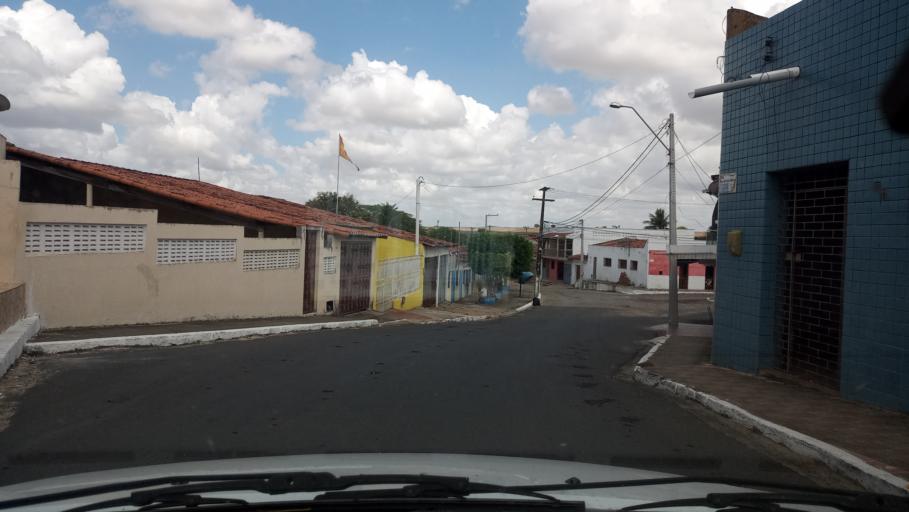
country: BR
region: Rio Grande do Norte
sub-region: Santo Antonio
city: Santo Antonio
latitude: -6.3485
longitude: -35.3758
